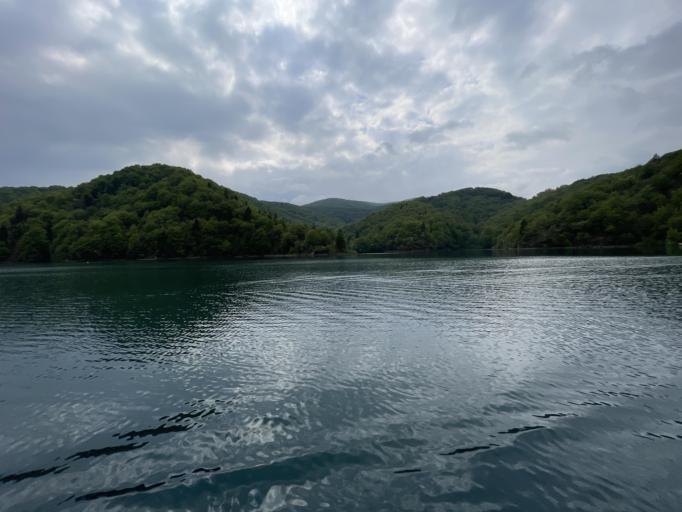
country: HR
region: Licko-Senjska
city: Jezerce
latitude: 44.8920
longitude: 15.6045
